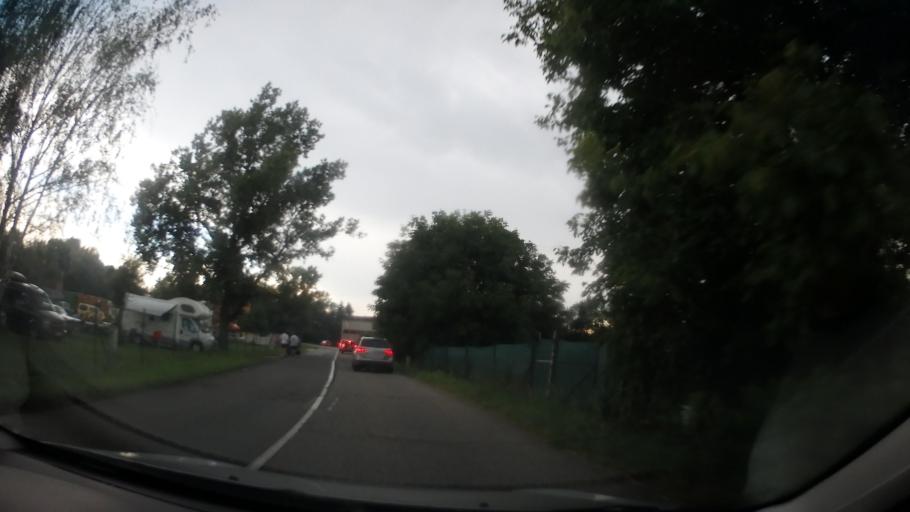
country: CZ
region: Olomoucky
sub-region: Okres Olomouc
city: Olomouc
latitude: 49.6091
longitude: 17.2432
